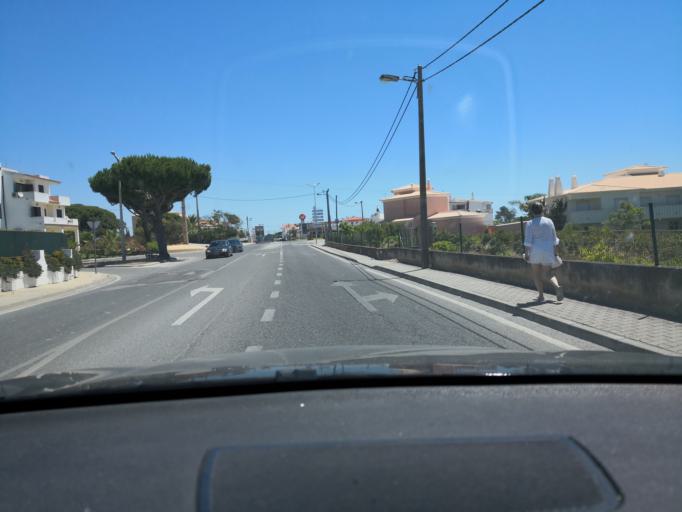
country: PT
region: Faro
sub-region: Albufeira
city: Ferreiras
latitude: 37.1041
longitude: -8.1959
